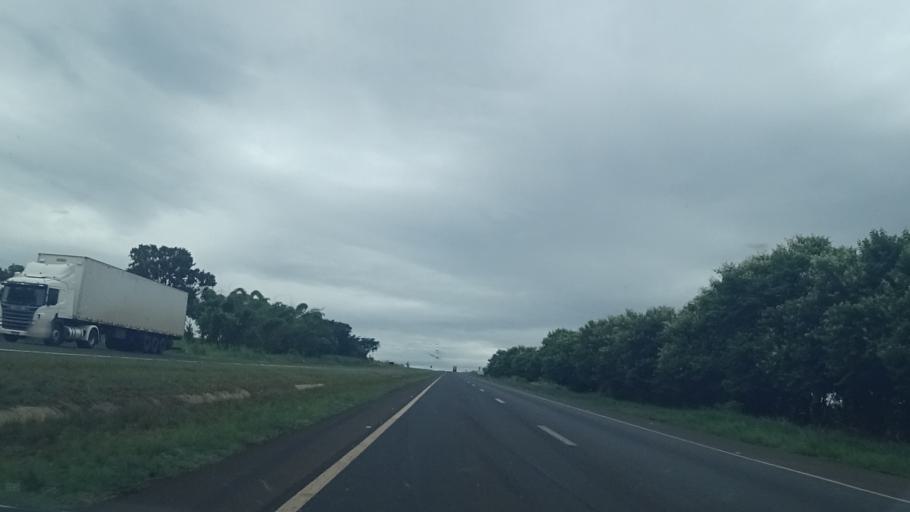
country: BR
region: Goias
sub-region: Goiatuba
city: Goiatuba
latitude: -18.0234
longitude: -49.2642
